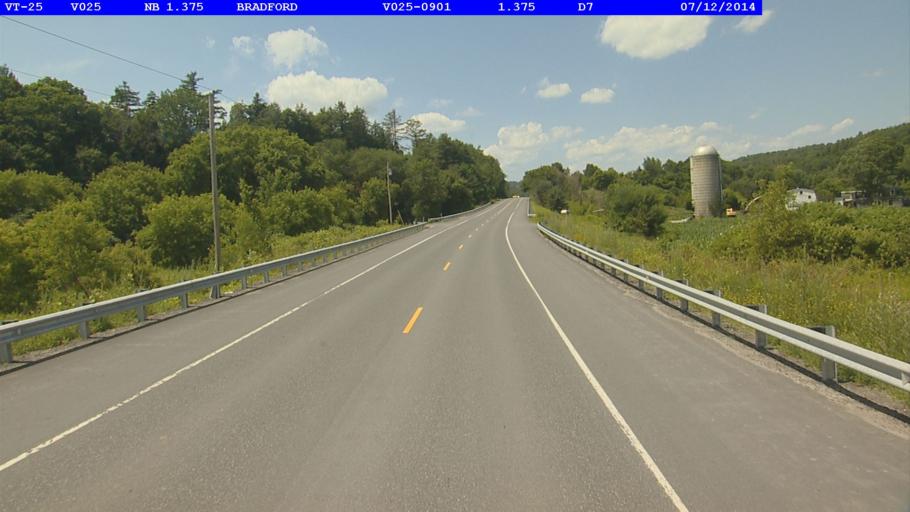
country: US
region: New Hampshire
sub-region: Grafton County
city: Orford
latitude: 43.9843
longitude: -72.1368
